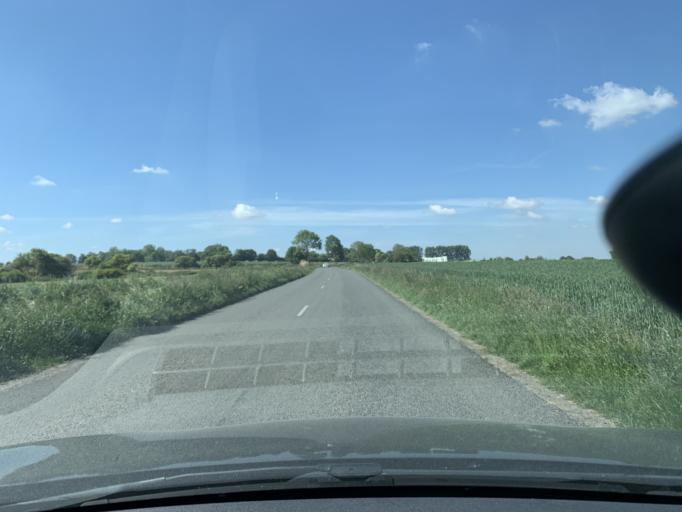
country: FR
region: Nord-Pas-de-Calais
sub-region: Departement du Pas-de-Calais
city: Oisy-le-Verger
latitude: 50.2573
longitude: 3.1315
